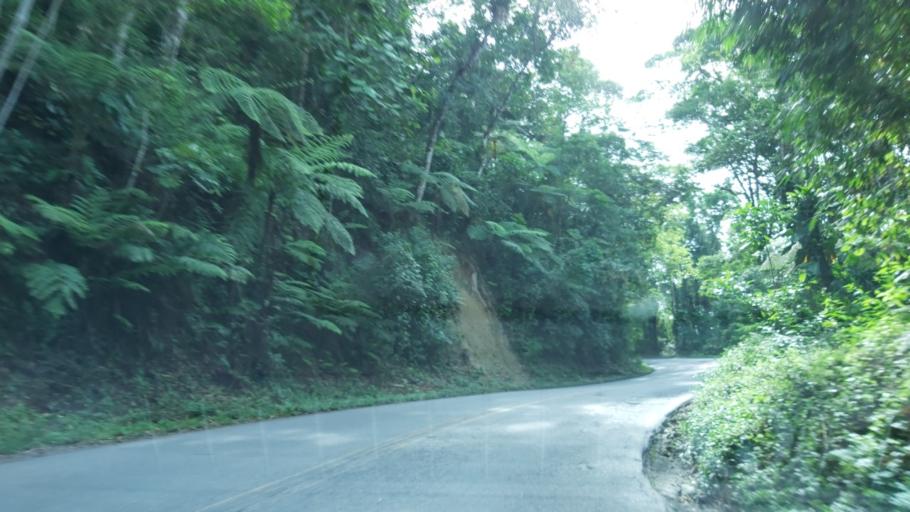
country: BR
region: Sao Paulo
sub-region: Juquia
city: Juquia
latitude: -24.0993
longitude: -47.6213
